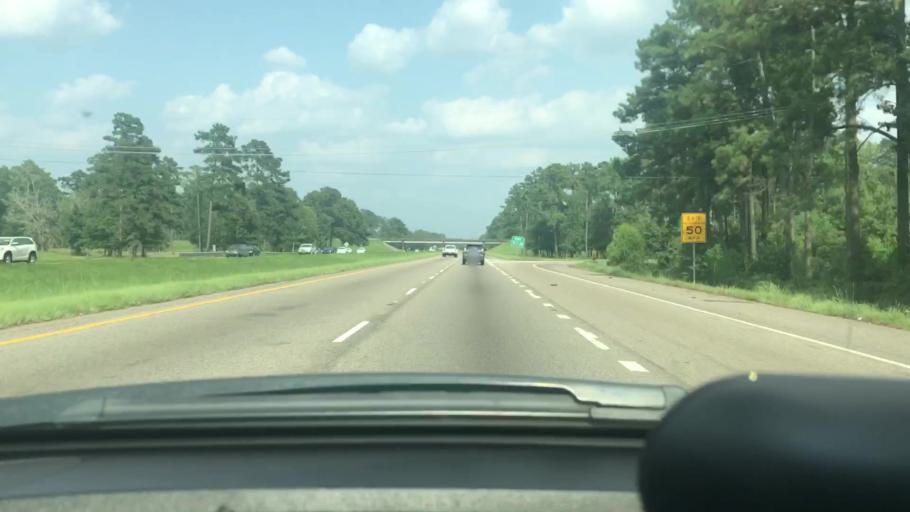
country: US
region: Louisiana
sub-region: Livingston Parish
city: Albany
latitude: 30.4773
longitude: -90.5834
